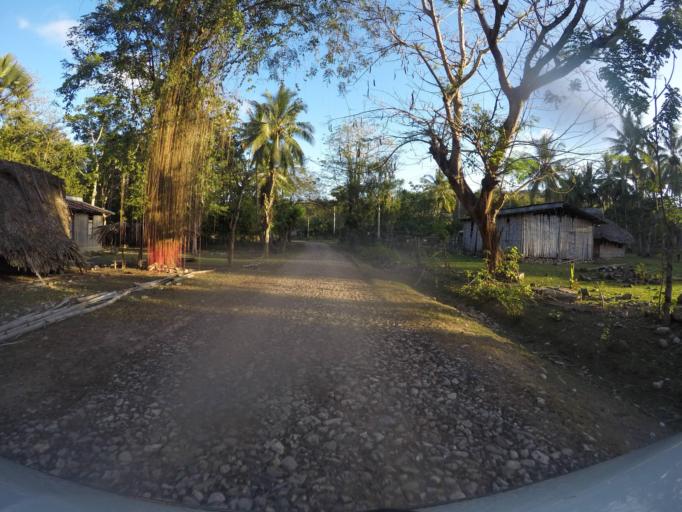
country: TL
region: Baucau
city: Venilale
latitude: -8.7314
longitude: 126.7093
